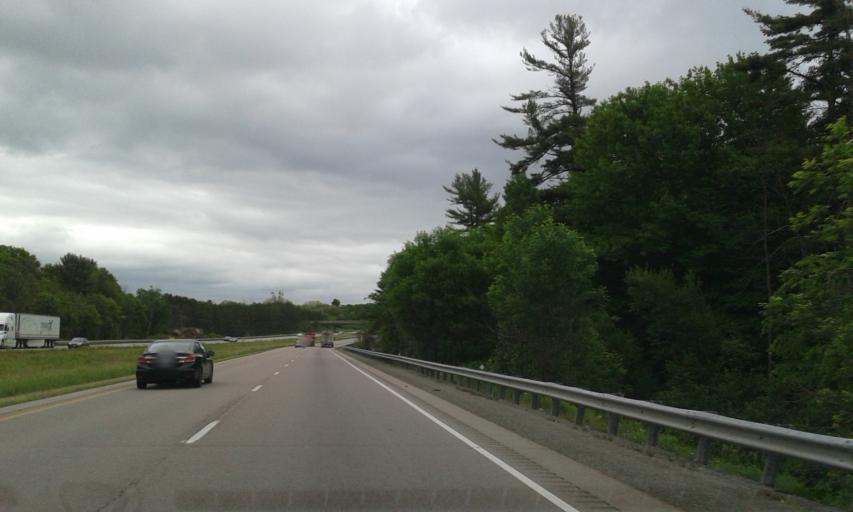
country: CA
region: Ontario
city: Brockville
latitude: 44.5192
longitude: -75.8104
